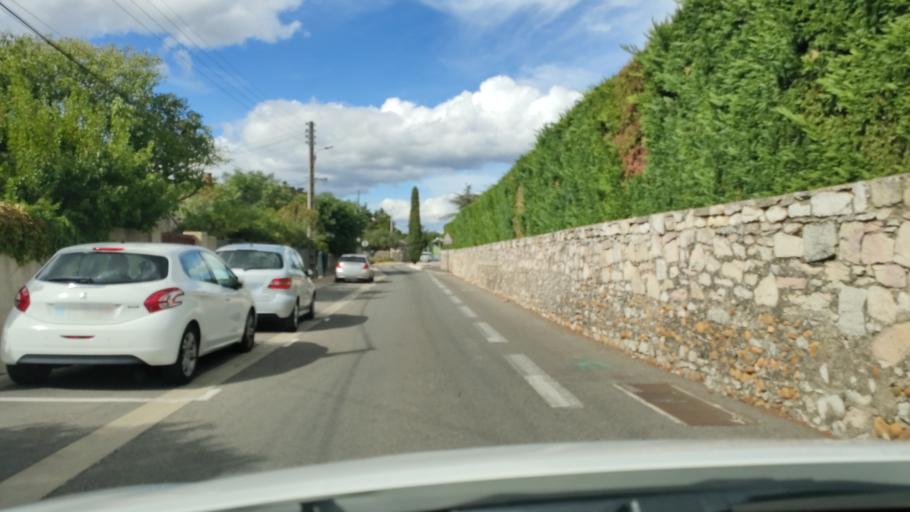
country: FR
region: Languedoc-Roussillon
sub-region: Departement du Gard
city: Villeneuve-les-Avignon
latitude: 43.9653
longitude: 4.7814
